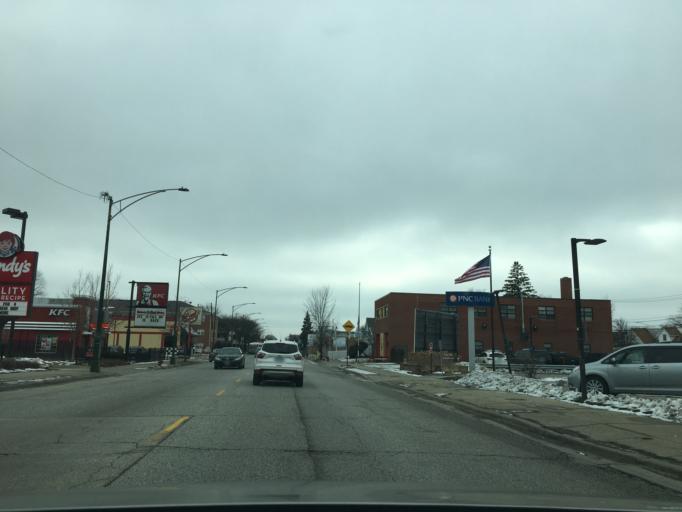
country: US
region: Illinois
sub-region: Cook County
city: Harwood Heights
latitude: 41.9521
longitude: -87.8072
